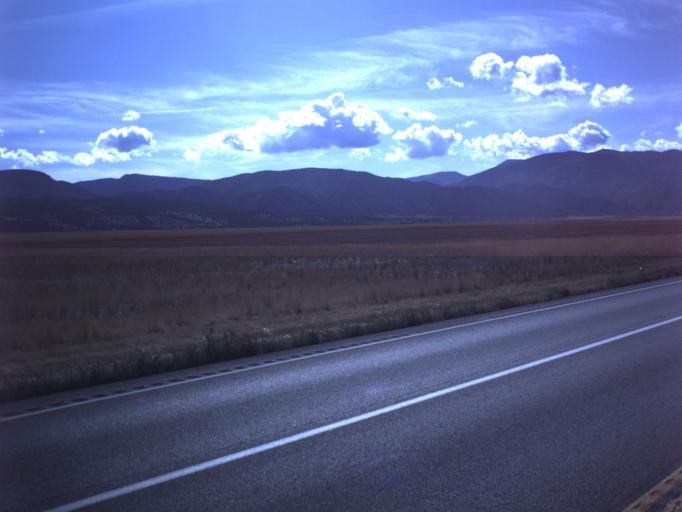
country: US
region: Utah
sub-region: Juab County
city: Nephi
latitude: 39.6174
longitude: -111.8619
